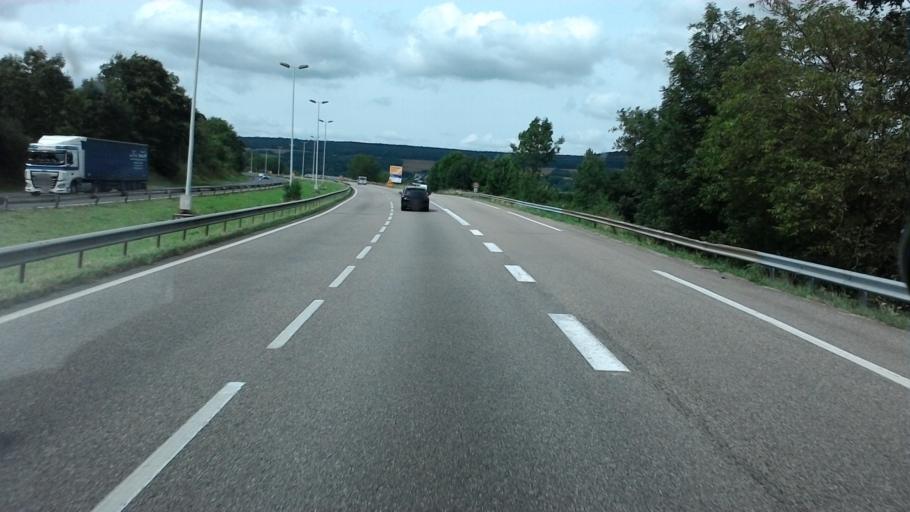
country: FR
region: Lorraine
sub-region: Departement de Meurthe-et-Moselle
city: Belleville
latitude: 48.8097
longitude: 6.1142
